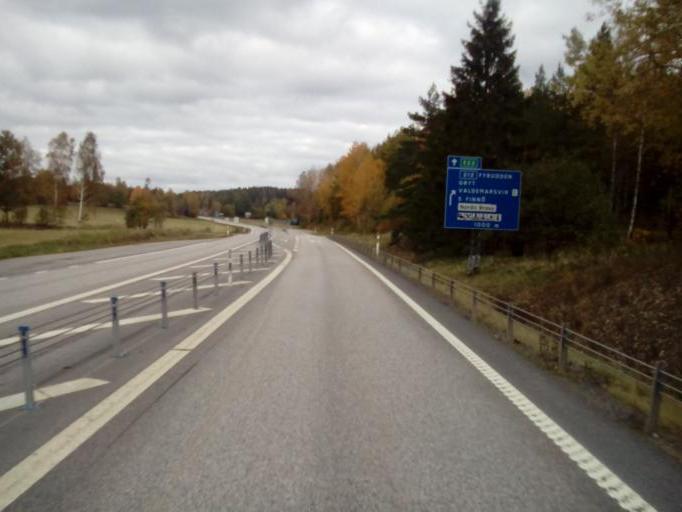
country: SE
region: OEstergoetland
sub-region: Valdemarsviks Kommun
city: Valdemarsvik
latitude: 58.2105
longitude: 16.5579
